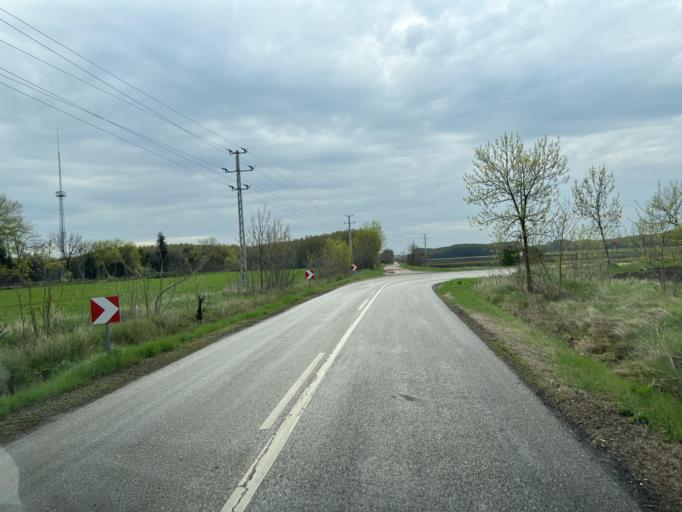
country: HU
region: Pest
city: Danszentmiklos
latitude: 47.2217
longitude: 19.5785
